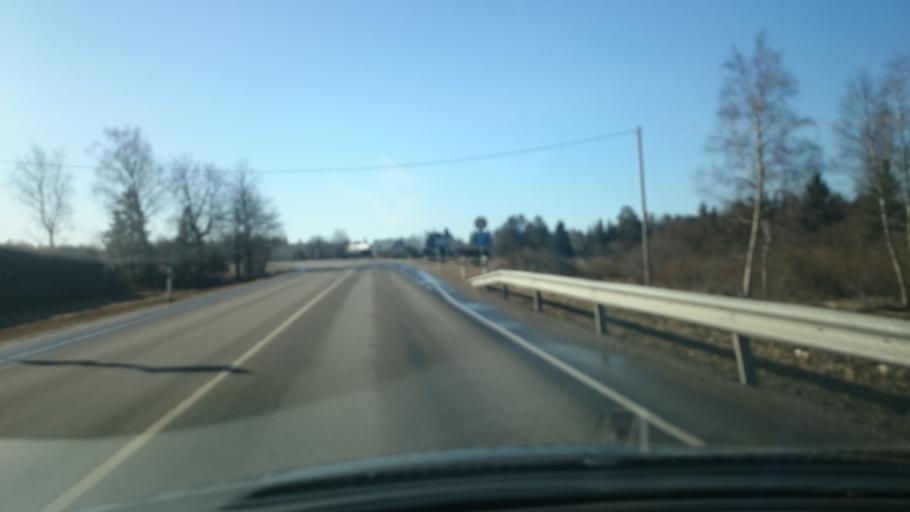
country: EE
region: Raplamaa
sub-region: Kohila vald
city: Kohila
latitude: 59.2531
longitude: 24.7416
